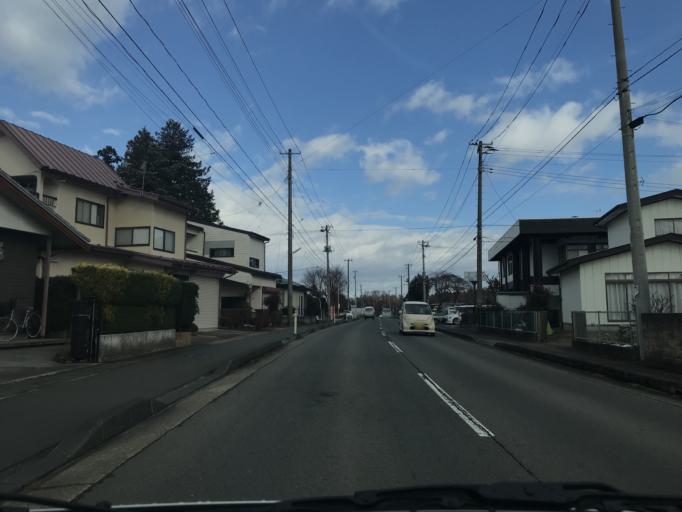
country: JP
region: Iwate
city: Mizusawa
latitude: 39.1171
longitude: 141.1378
